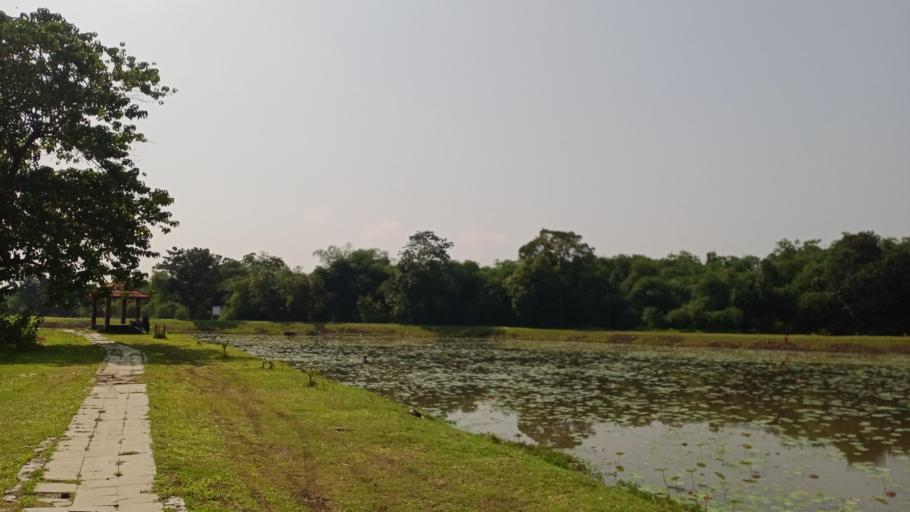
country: ID
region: West Java
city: Cileungsir
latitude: -6.3966
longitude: 107.0843
